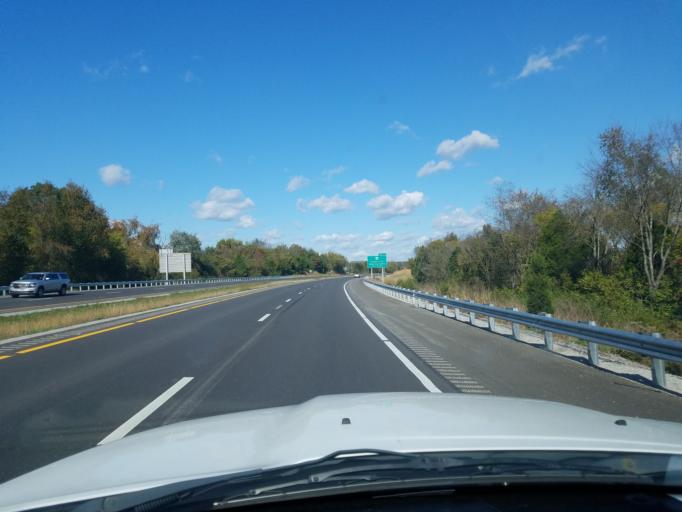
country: US
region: Kentucky
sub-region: Warren County
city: Bowling Green
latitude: 36.9491
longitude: -86.4936
